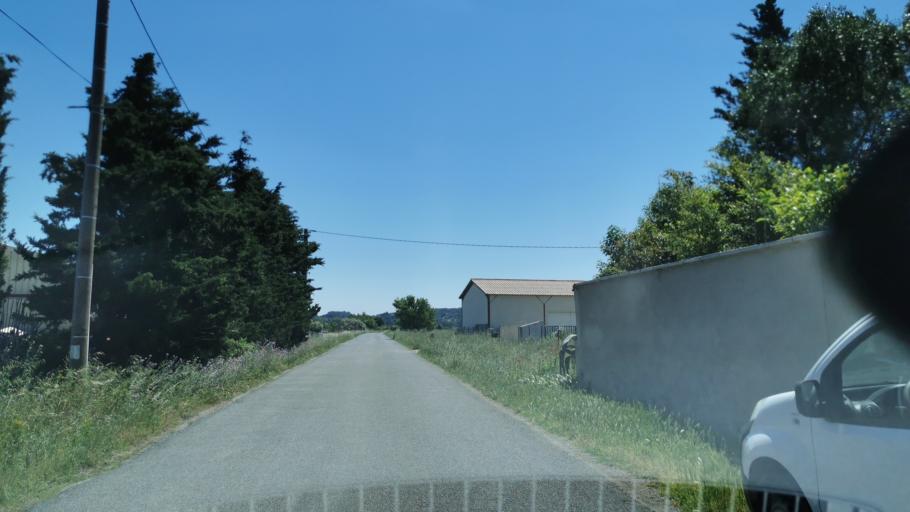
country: FR
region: Languedoc-Roussillon
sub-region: Departement de l'Aude
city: Marcorignan
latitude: 43.2444
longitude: 2.9090
